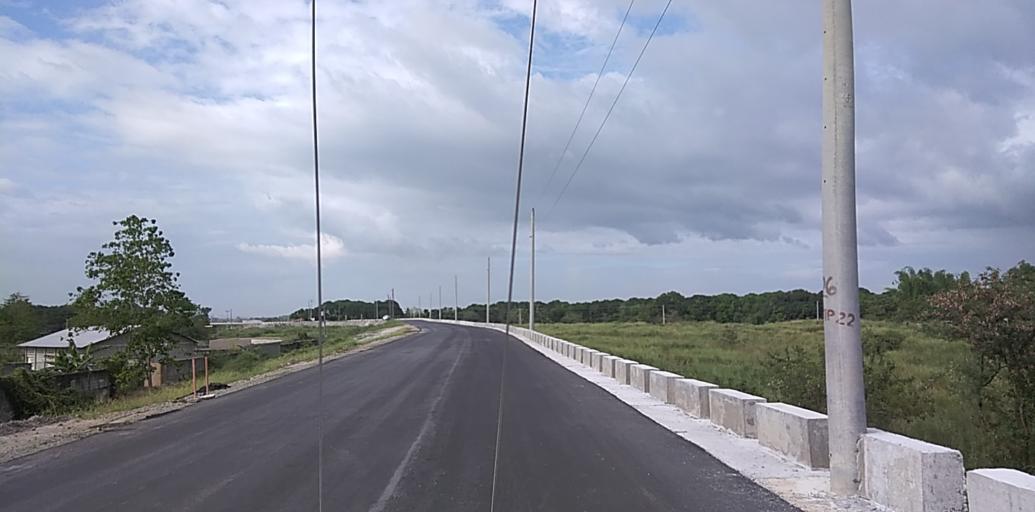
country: PH
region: Central Luzon
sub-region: Province of Pampanga
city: Porac
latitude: 15.0648
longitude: 120.5603
